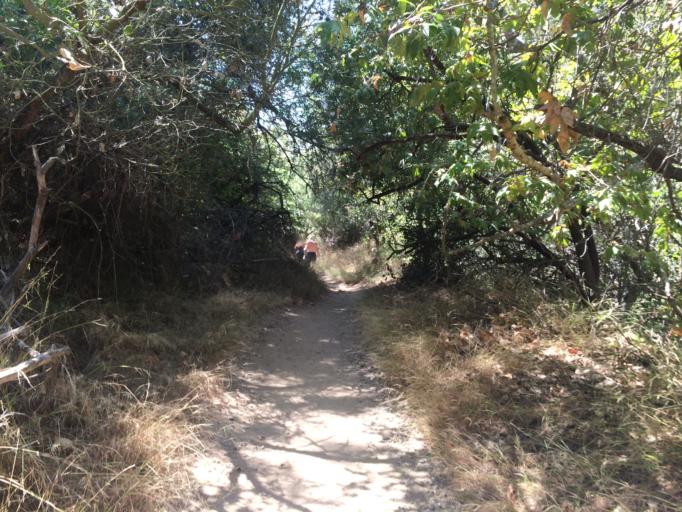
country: US
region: California
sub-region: Los Angeles County
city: Santa Monica
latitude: 34.0639
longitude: -118.5326
